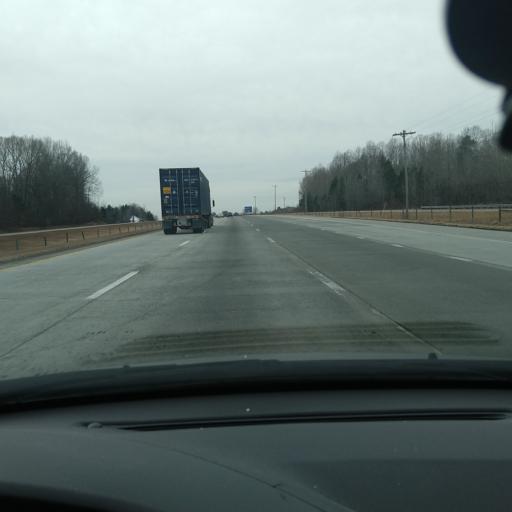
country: US
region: North Carolina
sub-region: Davidson County
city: Lexington
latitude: 35.8076
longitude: -80.2896
